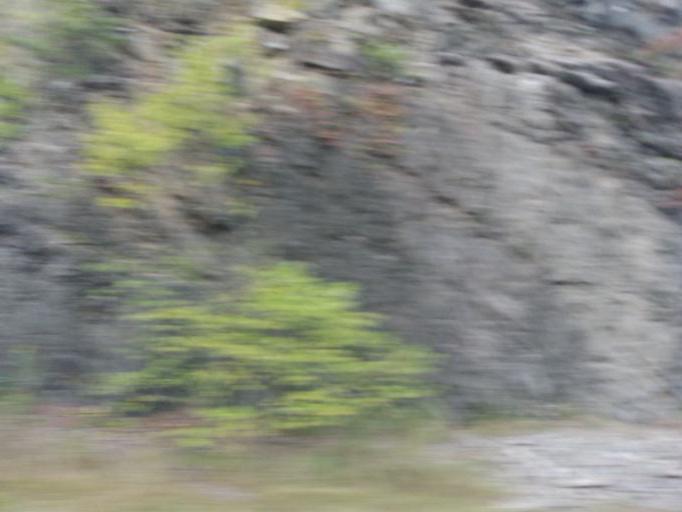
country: US
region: Tennessee
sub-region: Sevier County
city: Pigeon Forge
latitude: 35.7725
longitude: -83.6192
